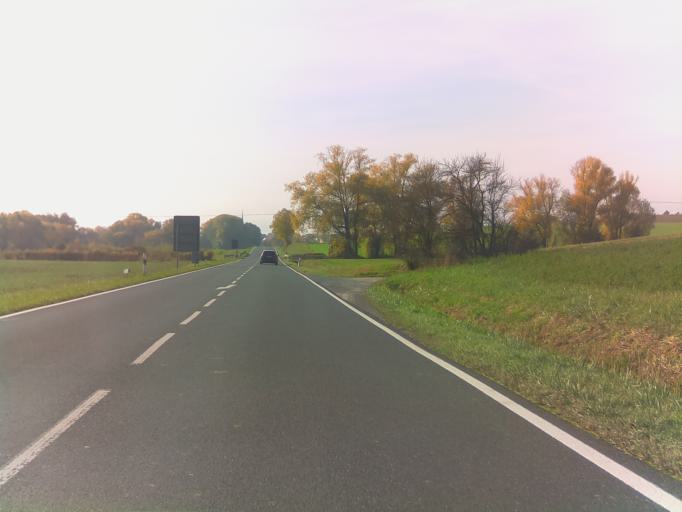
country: DE
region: Bavaria
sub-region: Regierungsbezirk Unterfranken
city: Prichsenstadt
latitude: 49.8435
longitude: 10.3481
